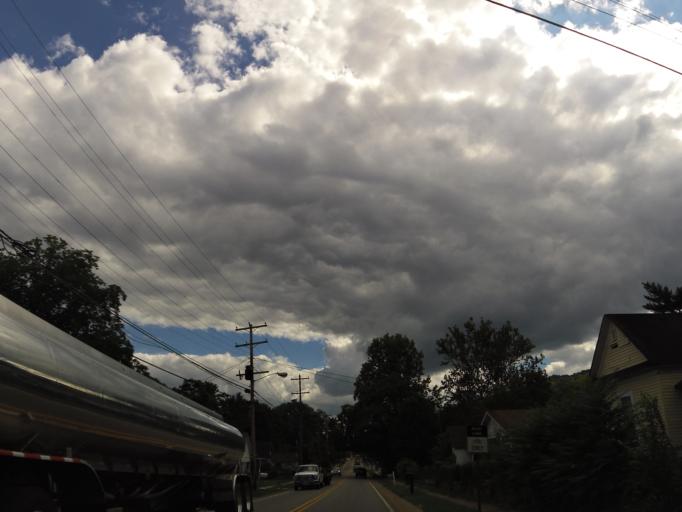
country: US
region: Tennessee
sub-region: Hamilton County
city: Lookout Mountain
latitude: 34.9882
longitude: -85.3313
